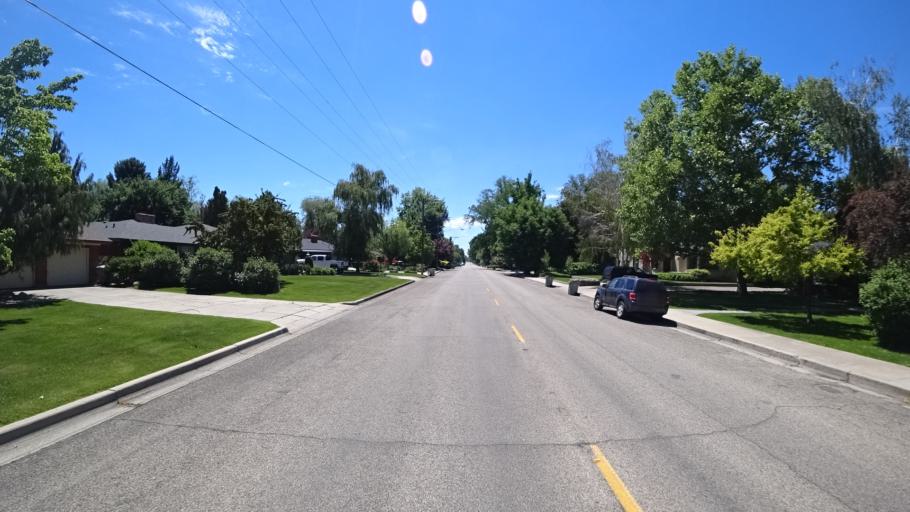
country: US
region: Idaho
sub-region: Ada County
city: Boise
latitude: 43.5961
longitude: -116.2236
